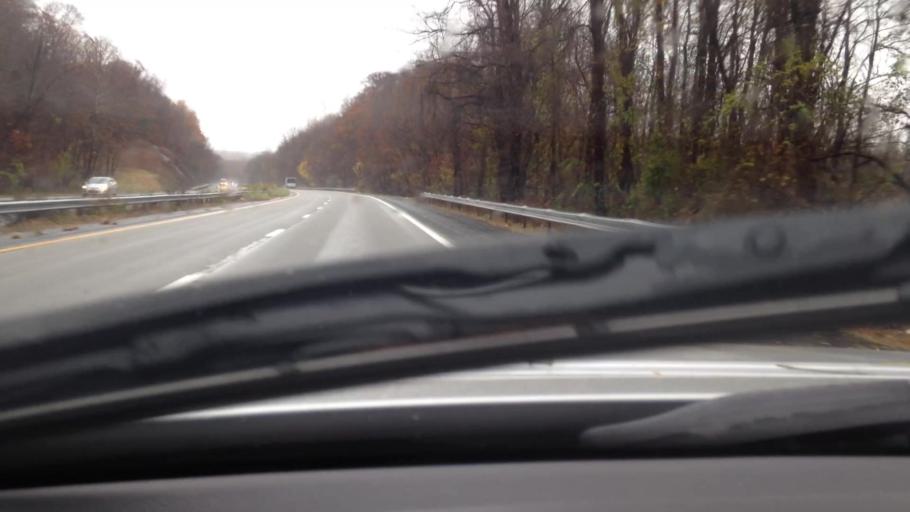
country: US
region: New York
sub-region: Westchester County
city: Crugers
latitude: 41.2445
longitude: -73.9195
